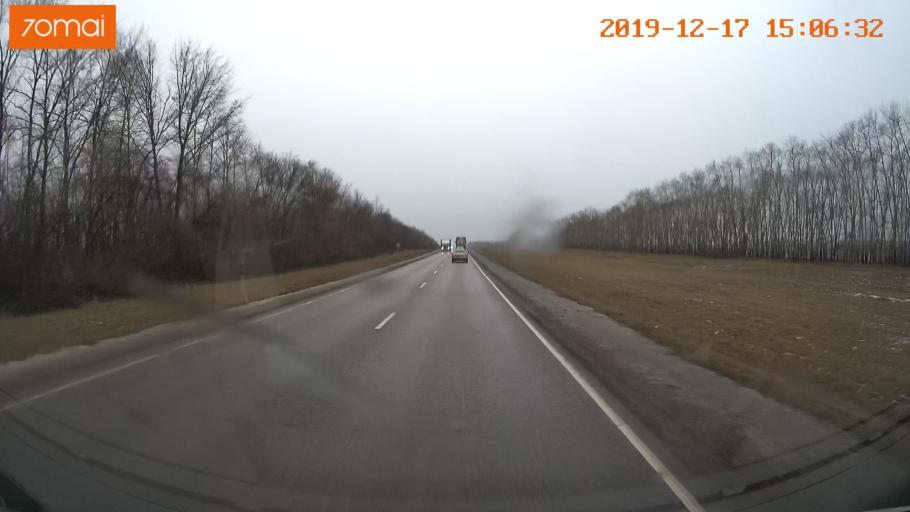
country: RU
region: Rjazan
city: Mikhaylov
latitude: 54.2583
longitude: 39.0981
